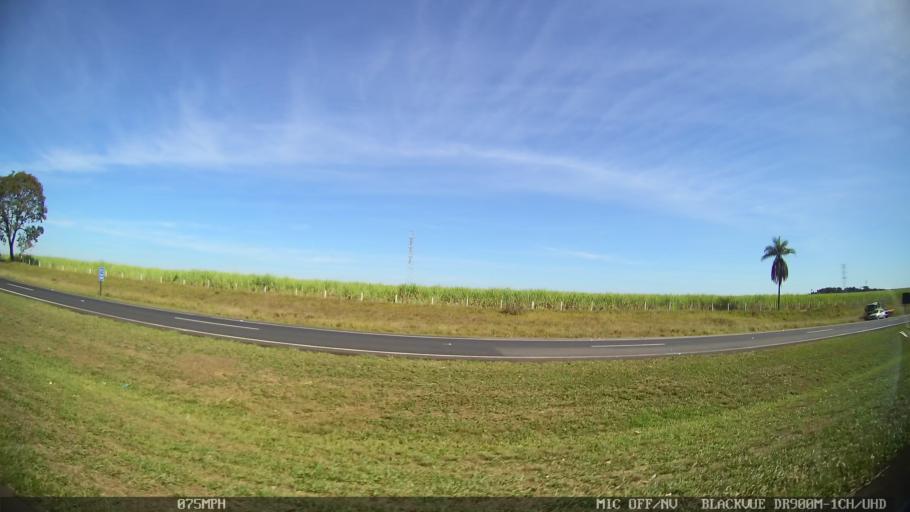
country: BR
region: Sao Paulo
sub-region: Porto Ferreira
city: Porto Ferreira
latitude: -21.8970
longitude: -47.4801
